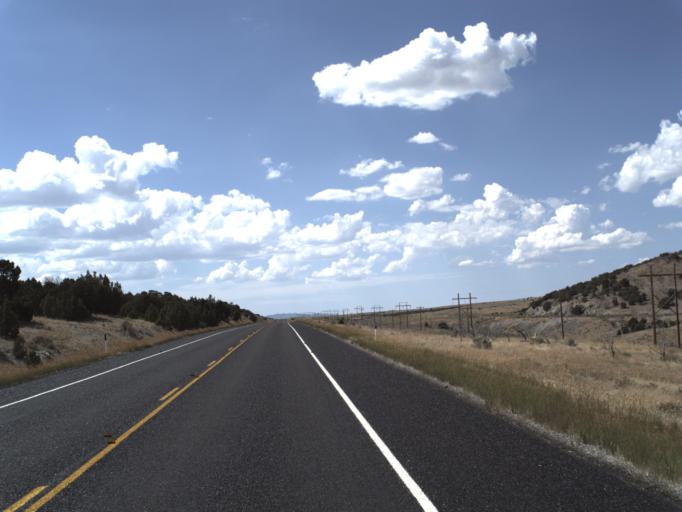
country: US
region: Idaho
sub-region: Minidoka County
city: Rupert
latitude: 41.9750
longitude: -113.1583
